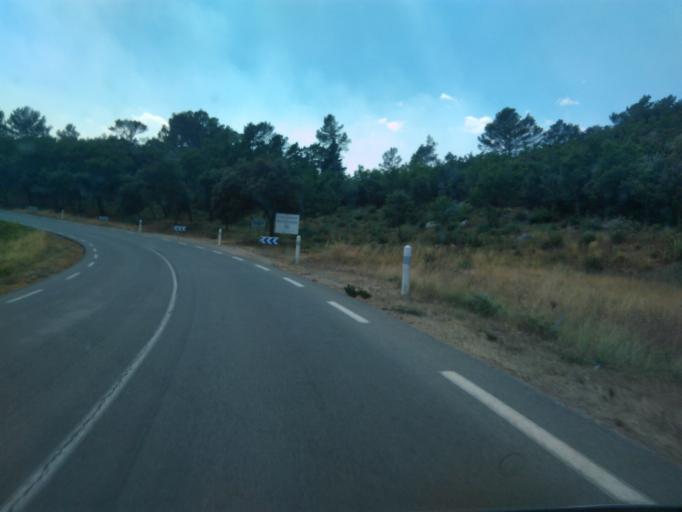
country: FR
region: Provence-Alpes-Cote d'Azur
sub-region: Departement du Var
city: Flassans-sur-Issole
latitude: 43.3875
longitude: 6.2473
